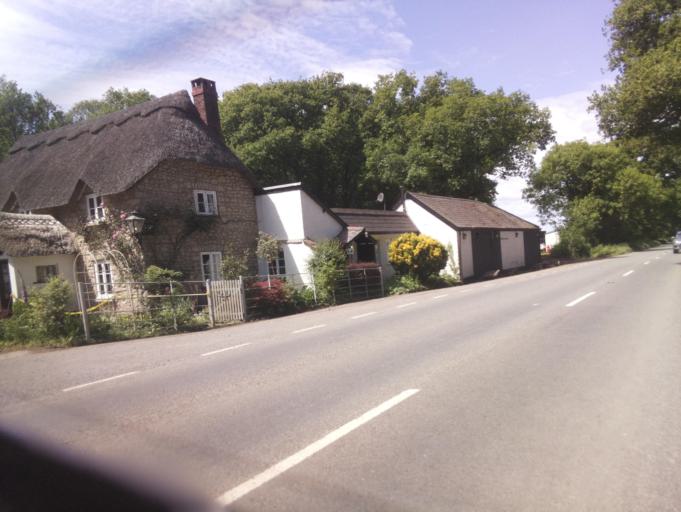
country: GB
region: England
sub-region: Devon
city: Uffculme
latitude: 50.8522
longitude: -3.3306
